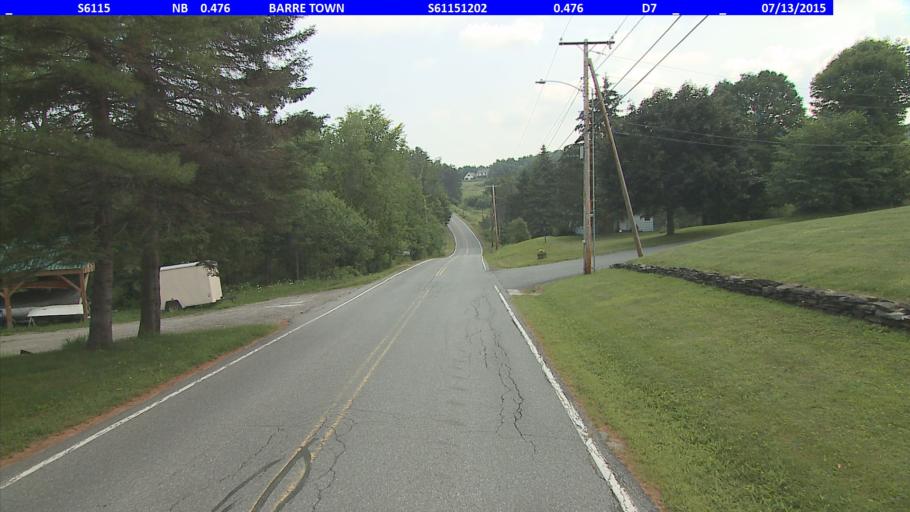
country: US
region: Vermont
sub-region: Washington County
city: Barre
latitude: 44.2061
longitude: -72.4818
